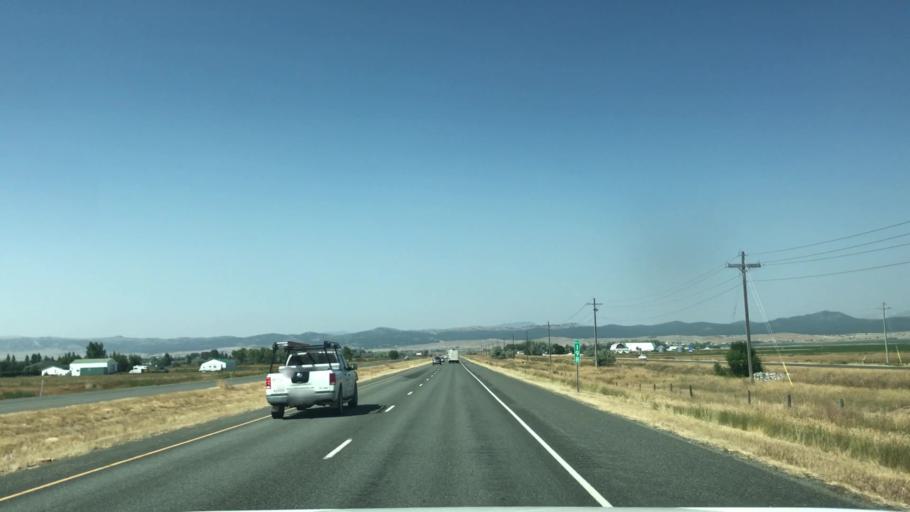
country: US
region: Montana
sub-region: Lewis and Clark County
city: Helena Valley West Central
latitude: 46.6738
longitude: -112.0115
